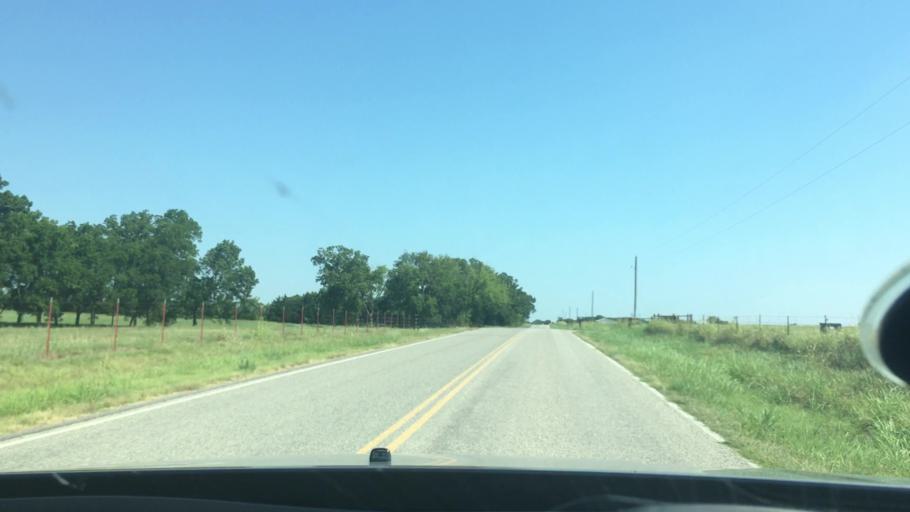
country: US
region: Oklahoma
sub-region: Johnston County
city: Tishomingo
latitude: 34.3049
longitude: -96.6184
